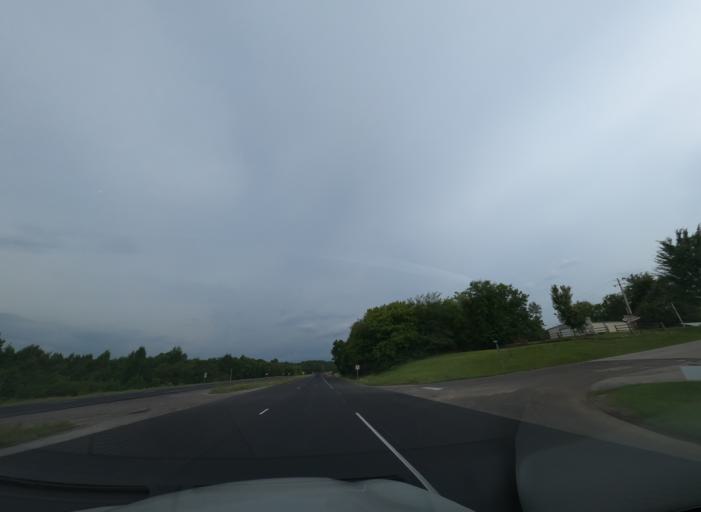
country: US
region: Alabama
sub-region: Colbert County
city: Cherokee
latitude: 34.7545
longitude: -87.9736
